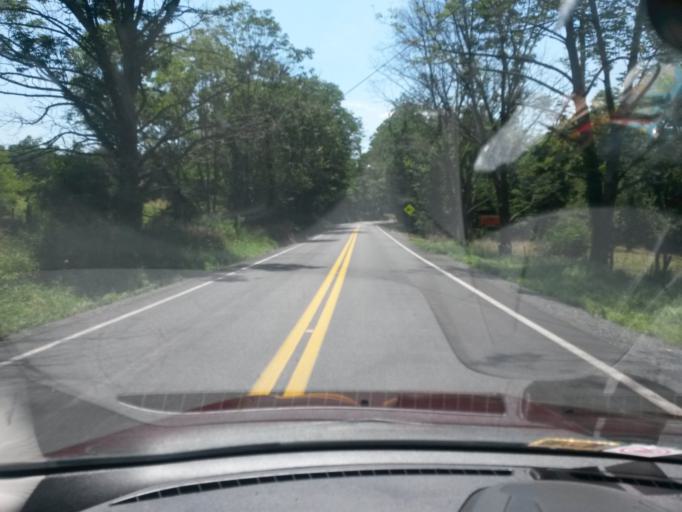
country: US
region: West Virginia
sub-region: Grant County
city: Petersburg
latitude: 39.2344
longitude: -79.1443
